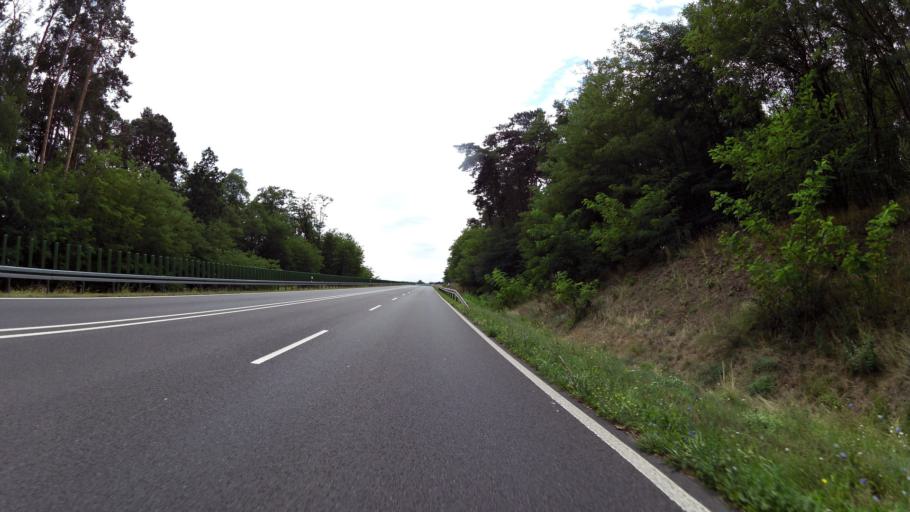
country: DE
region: Brandenburg
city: Neuzelle
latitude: 52.0364
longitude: 14.6777
